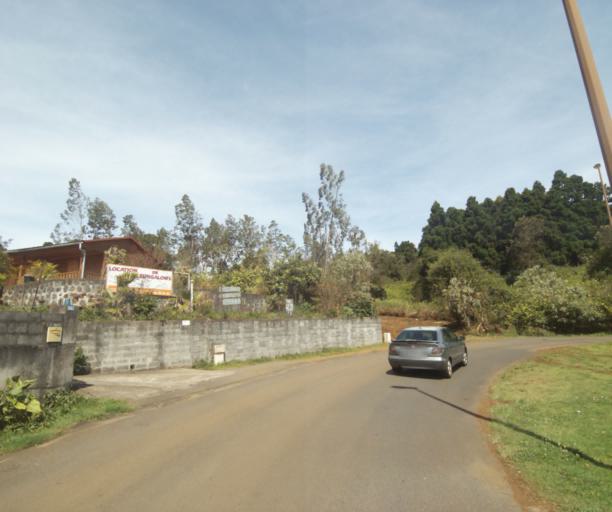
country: RE
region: Reunion
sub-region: Reunion
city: Trois-Bassins
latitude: -21.0461
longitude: 55.3329
